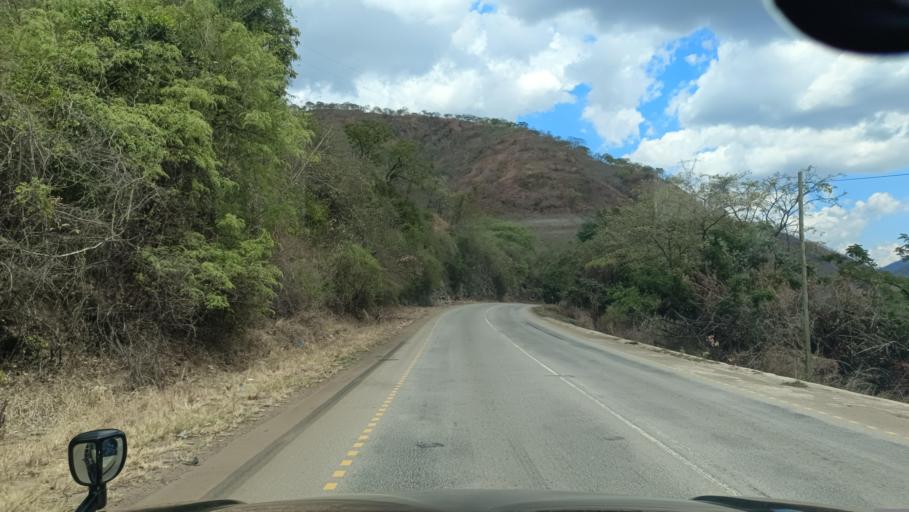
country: TZ
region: Morogoro
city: Kidatu
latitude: -7.5755
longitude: 36.7534
